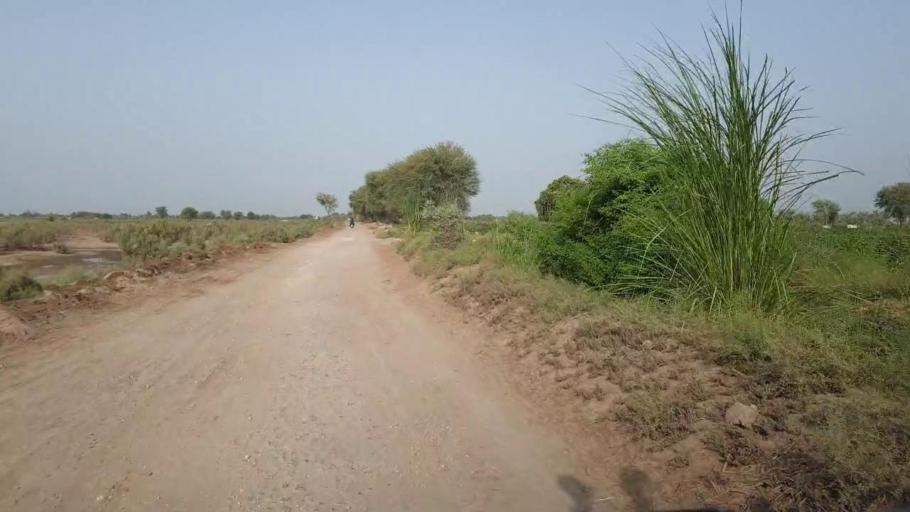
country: PK
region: Sindh
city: Daur
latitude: 26.3399
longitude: 68.2396
